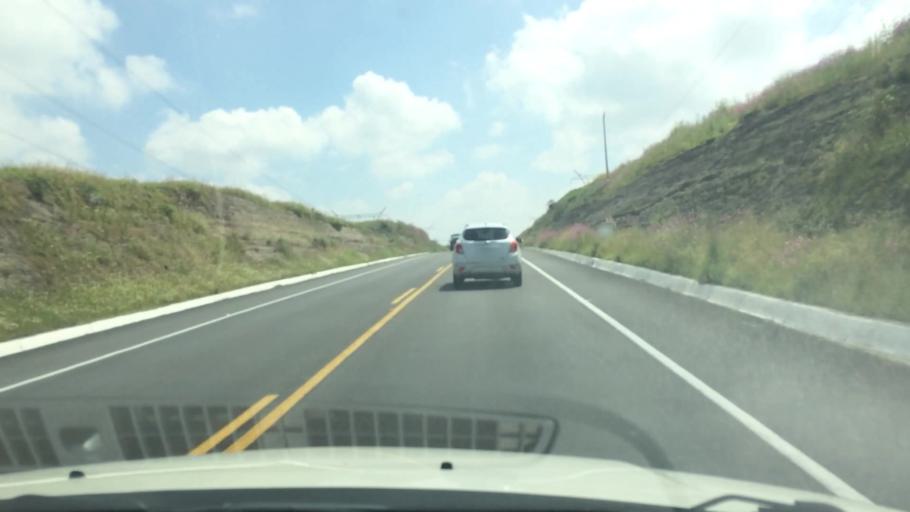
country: MX
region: Mexico
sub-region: Almoloya de Juarez
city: San Pedro de la Hortaliza (Ejido Almoloyan)
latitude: 19.3788
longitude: -99.8331
